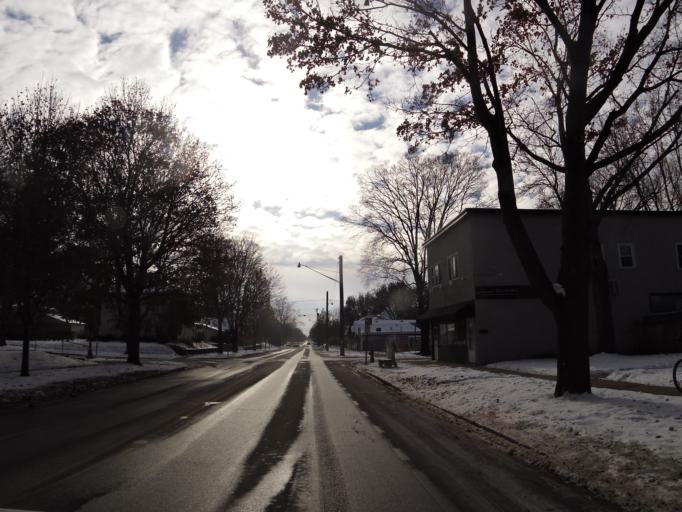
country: US
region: Minnesota
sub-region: Ramsey County
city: Falcon Heights
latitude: 44.9293
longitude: -93.1875
